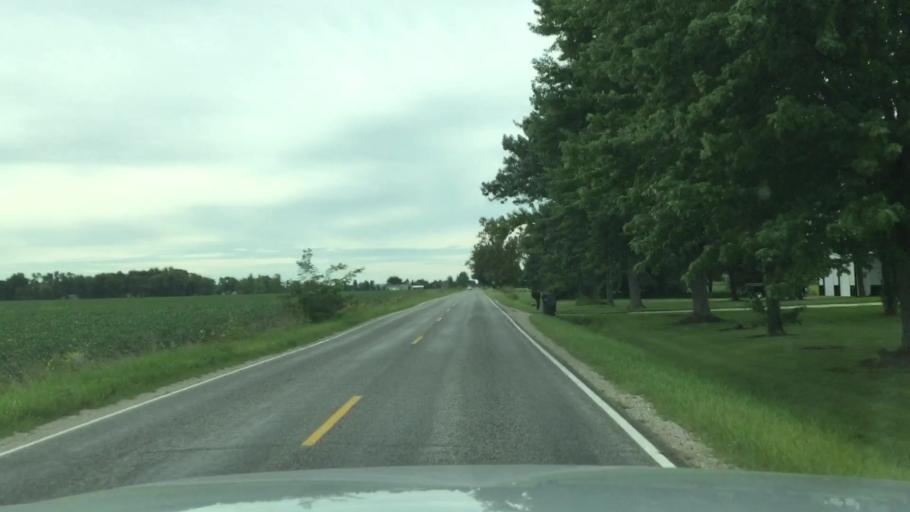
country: US
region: Michigan
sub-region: Shiawassee County
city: Durand
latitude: 43.0459
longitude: -83.9874
